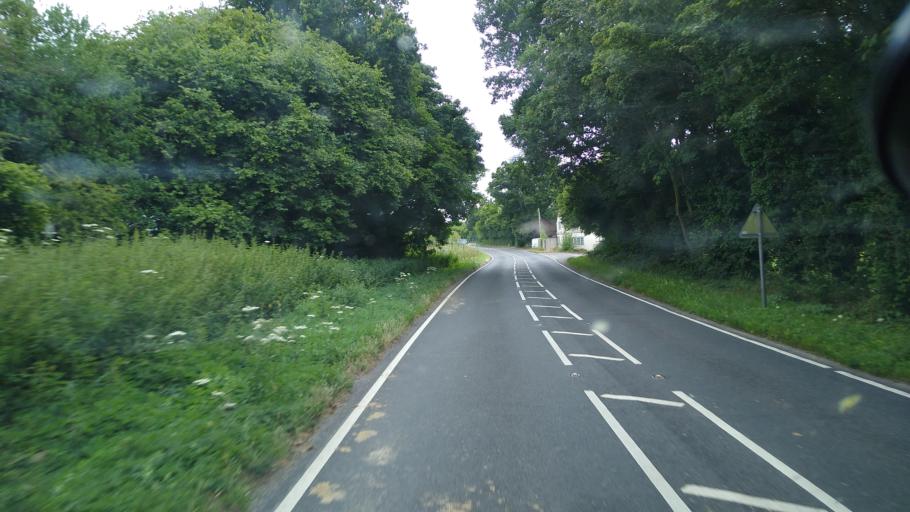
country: GB
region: England
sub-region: Hampshire
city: Liss
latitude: 51.0812
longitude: -0.9248
